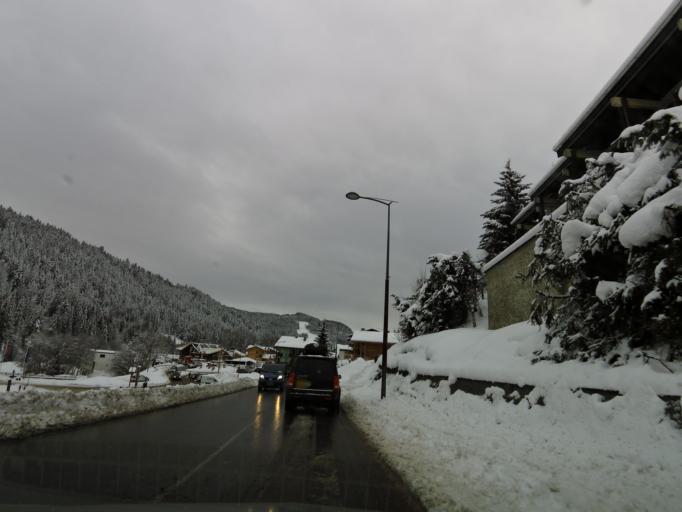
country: FR
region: Rhone-Alpes
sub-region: Departement de la Haute-Savoie
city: Les Gets
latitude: 46.1503
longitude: 6.6568
